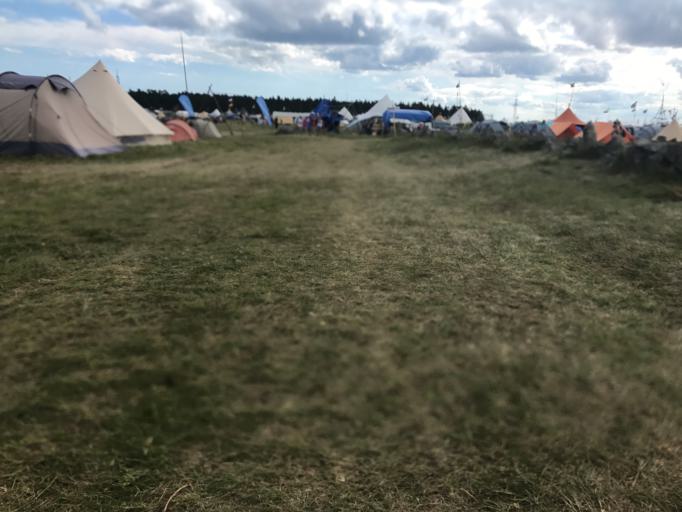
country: SE
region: Skane
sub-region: Kristianstads Kommun
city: Fjalkinge
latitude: 56.0063
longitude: 14.3025
